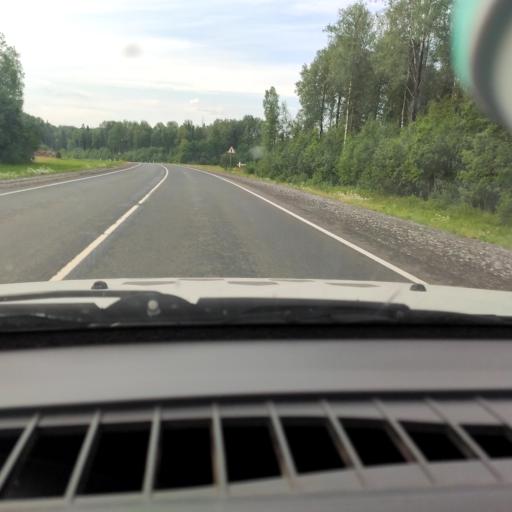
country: RU
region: Kirov
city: Kostino
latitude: 58.6859
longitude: 53.7381
